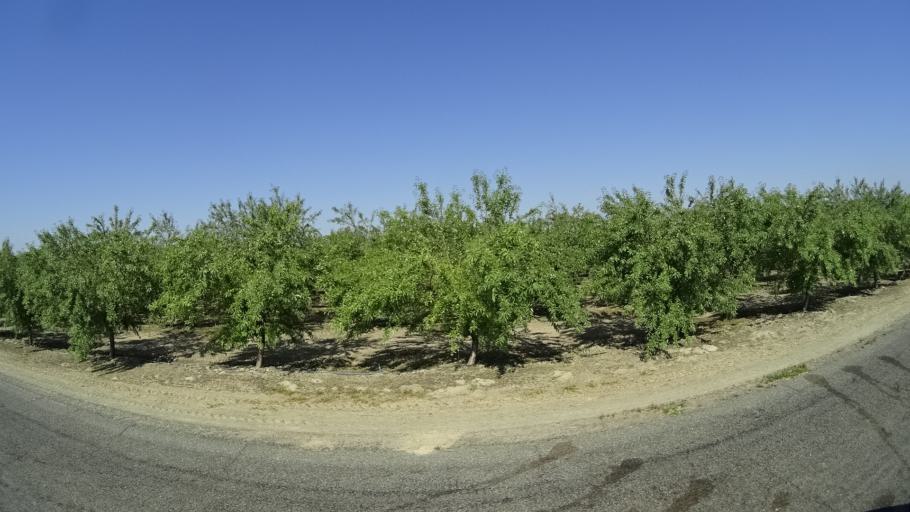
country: US
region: California
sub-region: Kings County
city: Hanford
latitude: 36.3882
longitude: -119.5470
